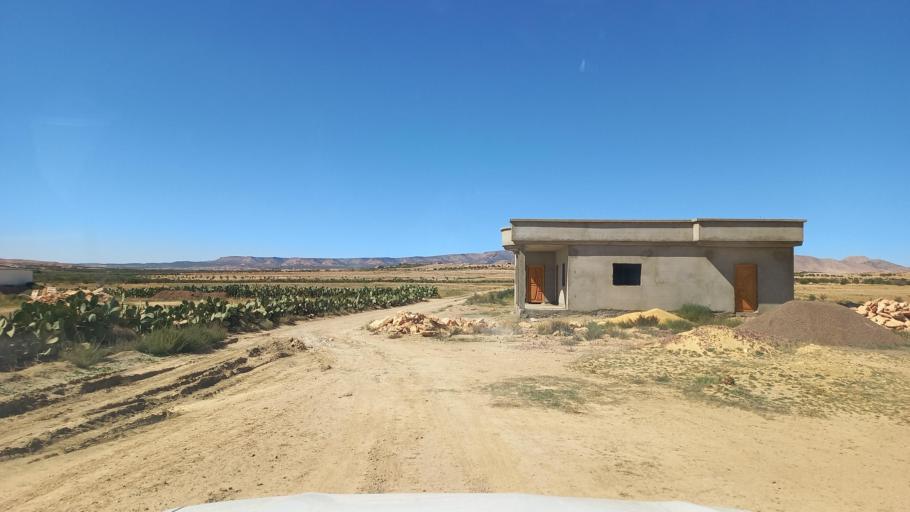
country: TN
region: Al Qasrayn
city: Sbiba
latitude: 35.3688
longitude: 9.0855
